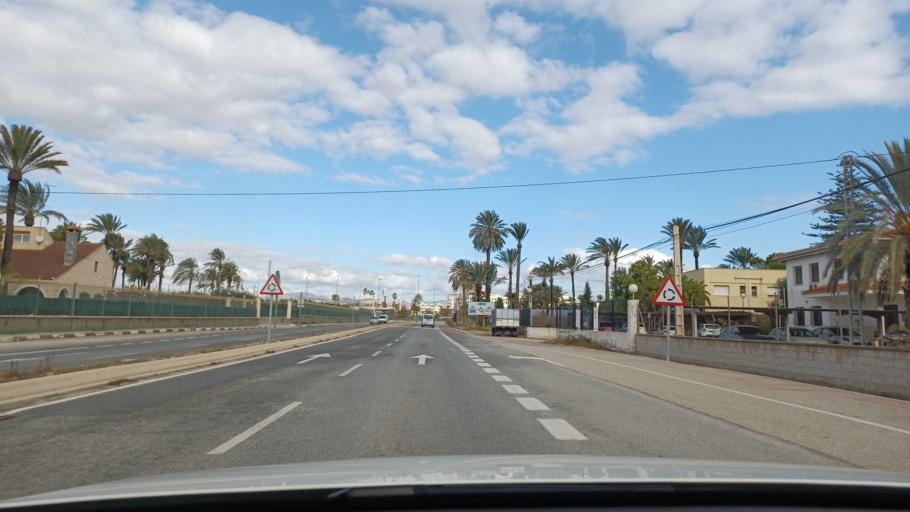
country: ES
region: Valencia
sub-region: Provincia de Alicante
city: Elche
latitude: 38.2470
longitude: -0.6982
